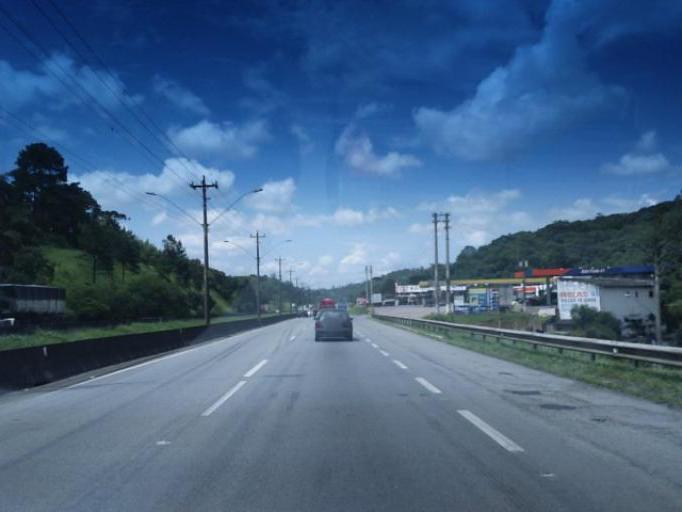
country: BR
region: Sao Paulo
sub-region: Itapecerica Da Serra
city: Itapecerica da Serra
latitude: -23.7626
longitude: -46.9058
